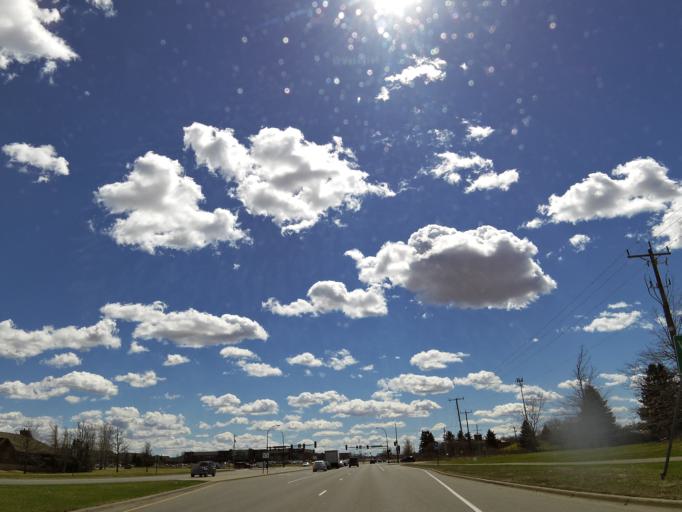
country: US
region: Minnesota
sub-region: Washington County
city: Woodbury
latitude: 44.9214
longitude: -92.9343
